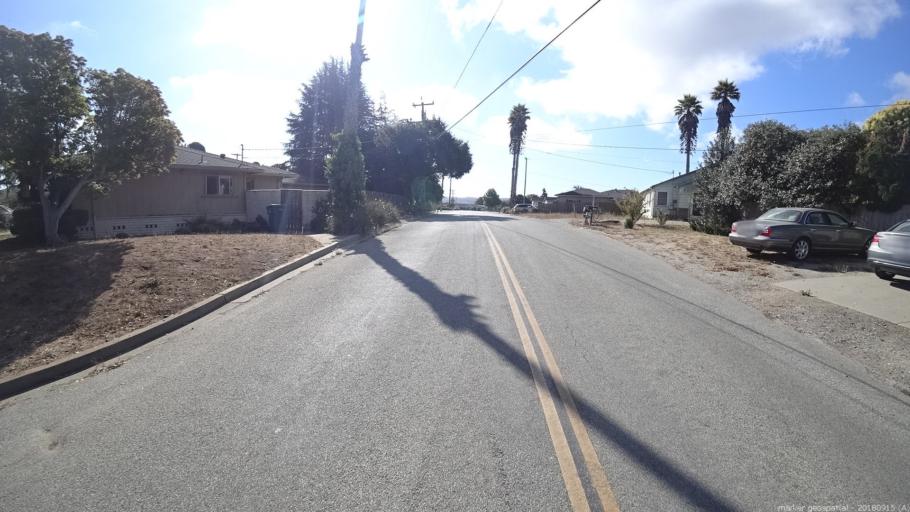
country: US
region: California
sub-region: Monterey County
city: Las Lomas
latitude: 36.8774
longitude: -121.7521
